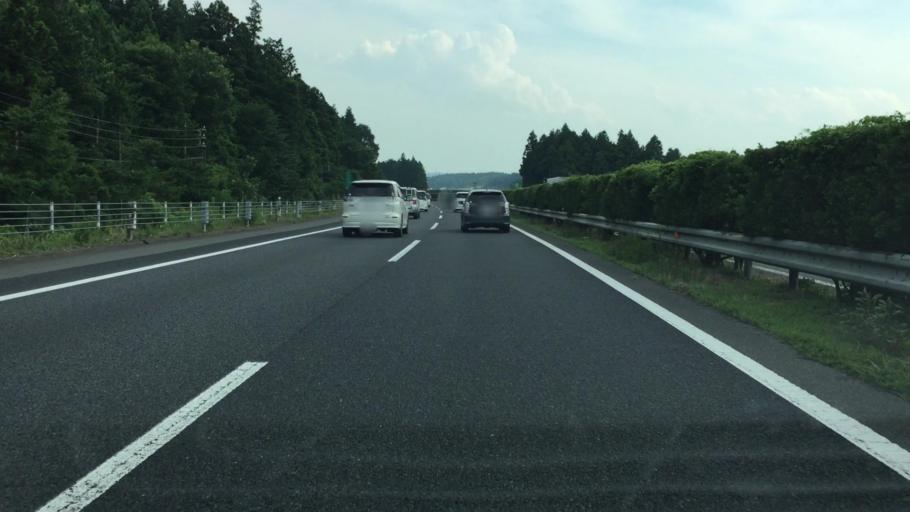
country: JP
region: Tochigi
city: Yaita
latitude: 36.8667
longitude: 139.9126
